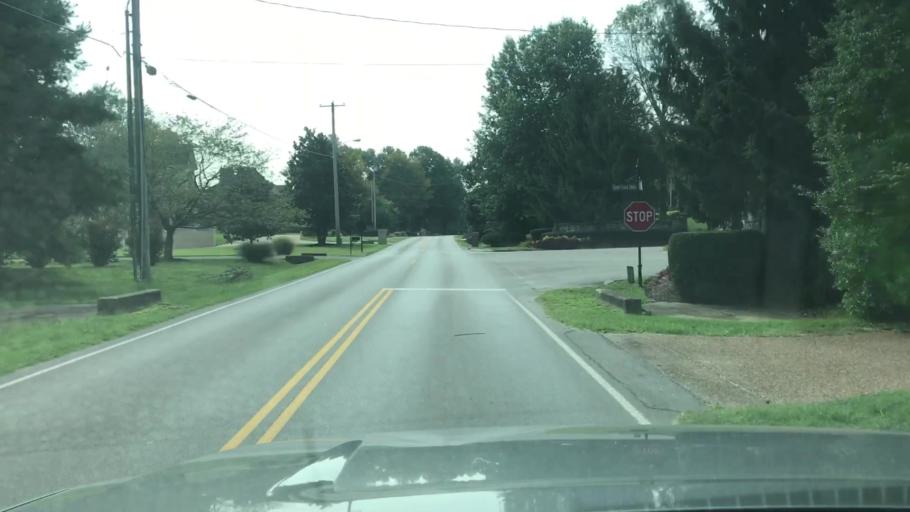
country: US
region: Tennessee
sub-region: Davidson County
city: Forest Hills
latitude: 36.0299
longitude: -86.8264
